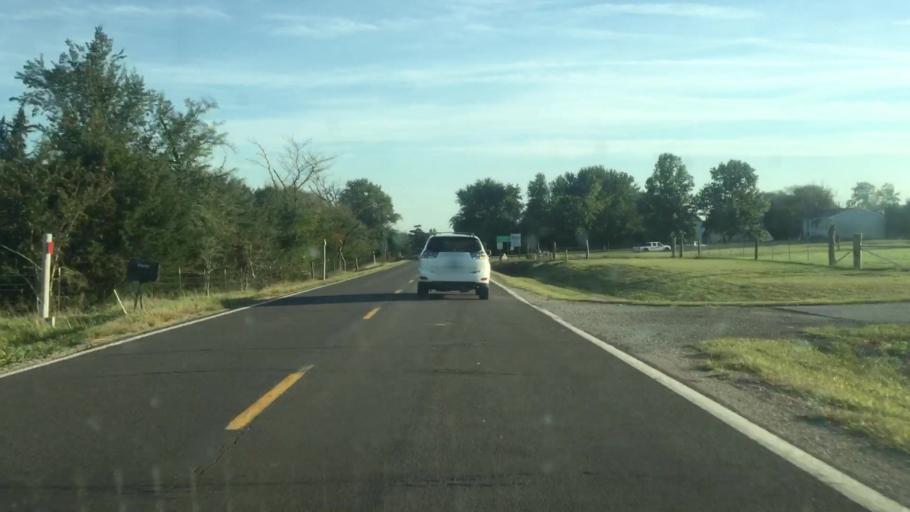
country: US
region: Kansas
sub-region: Brown County
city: Horton
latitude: 39.5583
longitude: -95.5247
